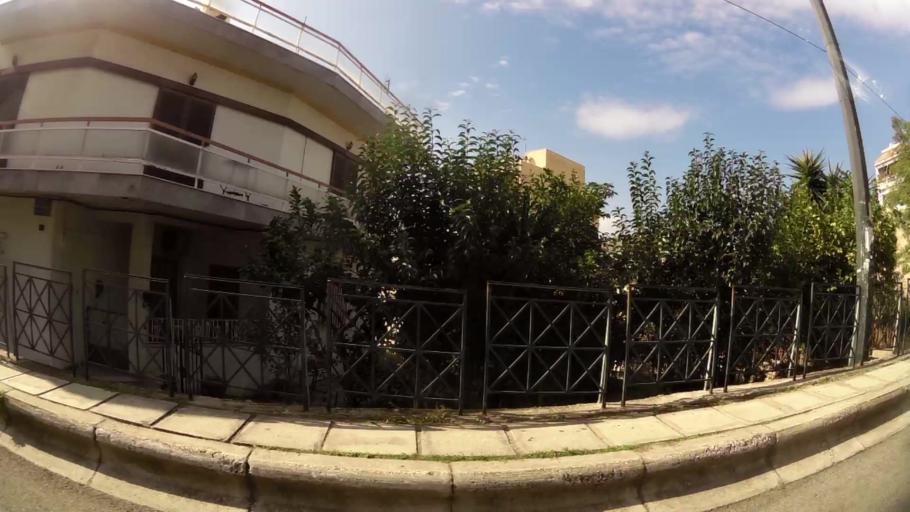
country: GR
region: Attica
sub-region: Nomos Piraios
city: Keratsini
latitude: 37.9616
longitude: 23.6138
